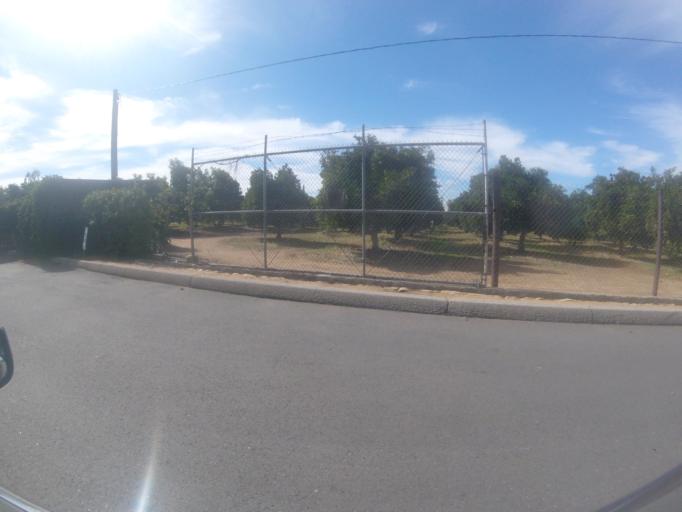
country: US
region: California
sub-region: San Bernardino County
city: Mentone
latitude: 34.0539
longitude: -117.1498
